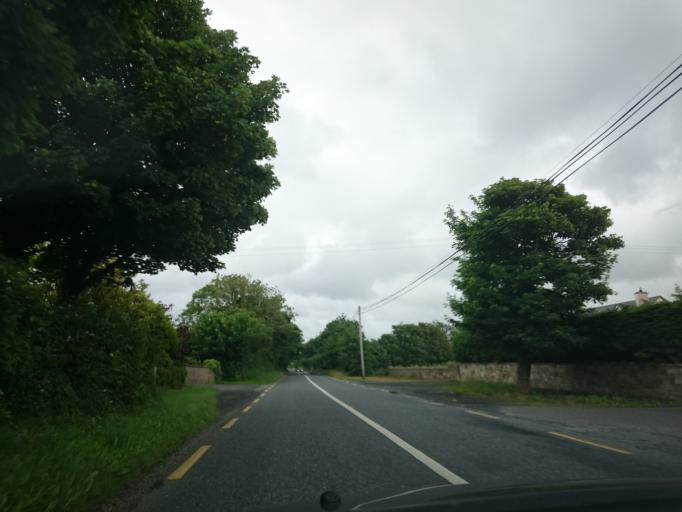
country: IE
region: Connaught
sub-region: Maigh Eo
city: Ballina
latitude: 54.2262
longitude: -9.2490
